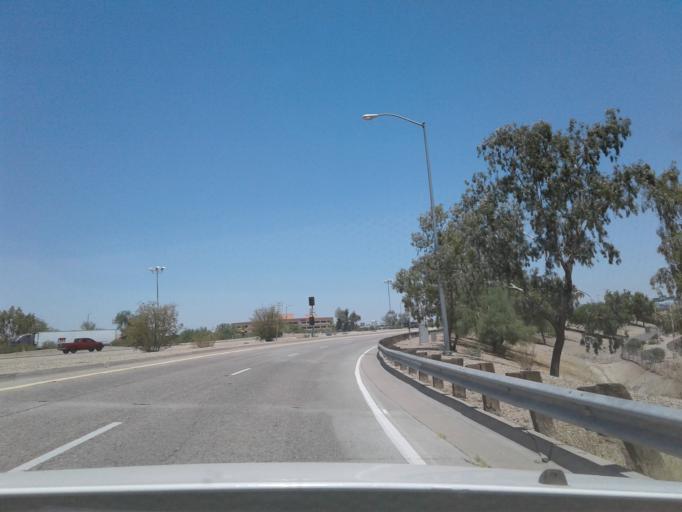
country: US
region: Arizona
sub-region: Maricopa County
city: Phoenix
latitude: 33.4382
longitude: -112.0362
